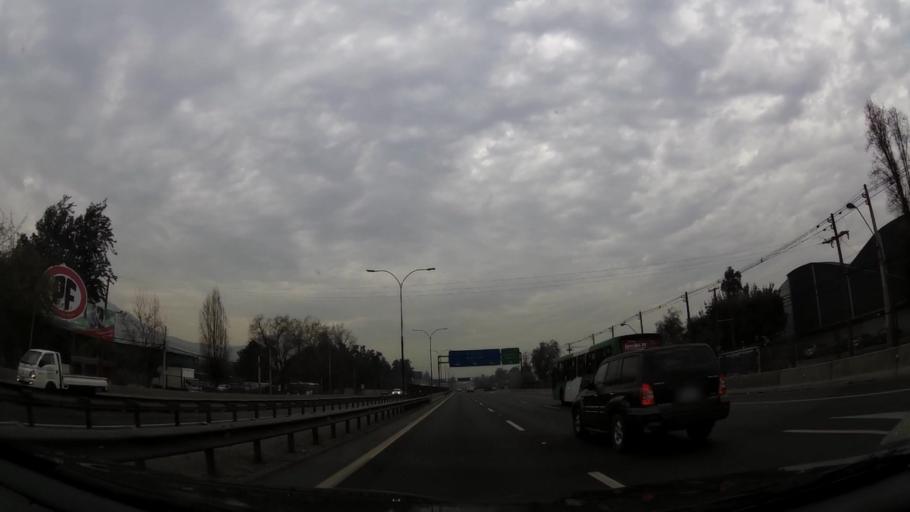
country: CL
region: Santiago Metropolitan
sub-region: Provincia de Santiago
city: Lo Prado
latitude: -33.3957
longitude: -70.6863
